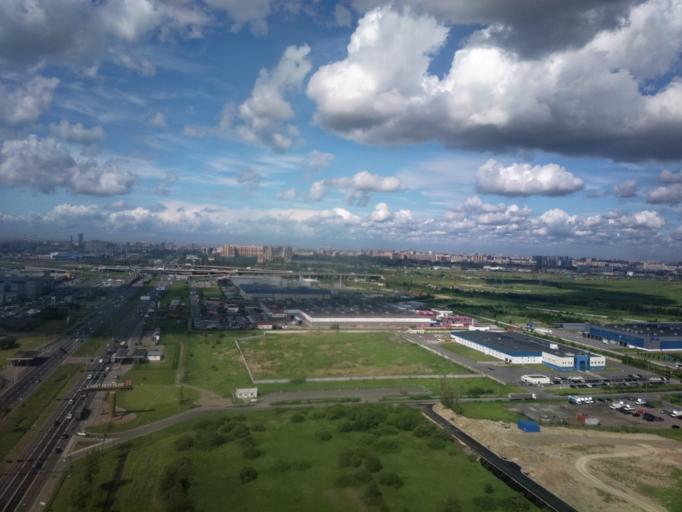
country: RU
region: St.-Petersburg
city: Shushary
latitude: 59.7976
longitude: 30.3283
